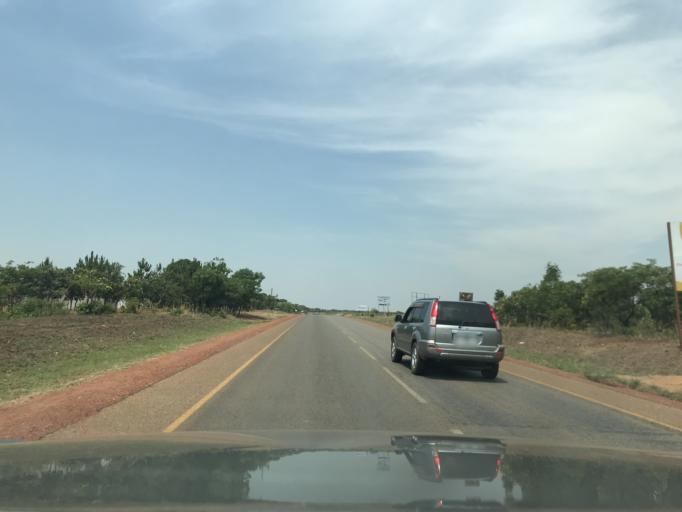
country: ZM
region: Northern
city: Kasama
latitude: -10.2179
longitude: 31.1433
